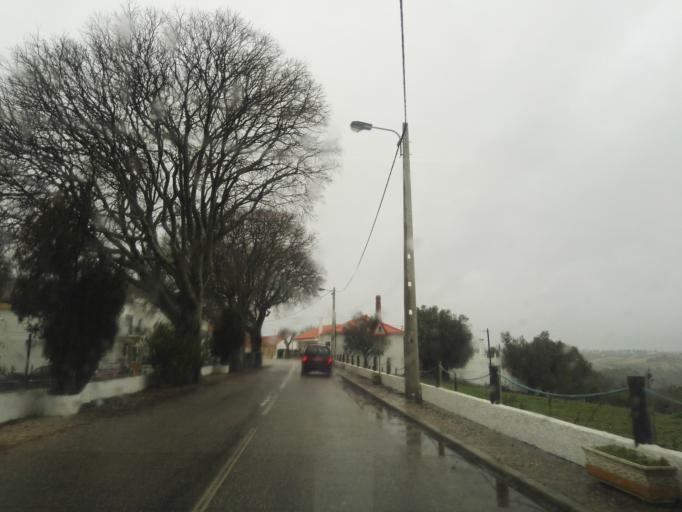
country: PT
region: Santarem
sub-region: Santarem
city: Alcanede
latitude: 39.3129
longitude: -8.7819
